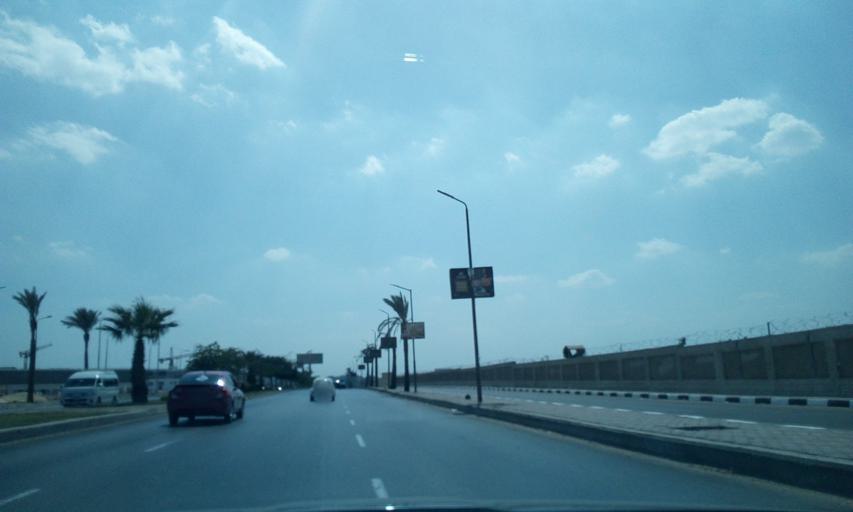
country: EG
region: Muhafazat al Qahirah
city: Cairo
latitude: 30.0860
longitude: 31.3662
